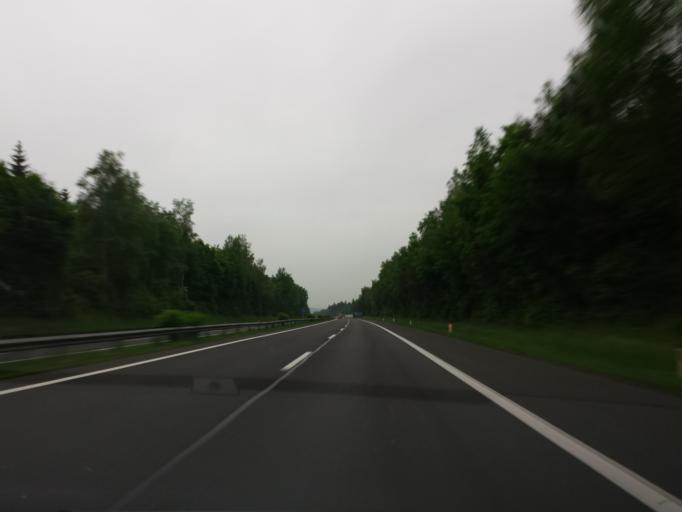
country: AT
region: Styria
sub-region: Politischer Bezirk Hartberg-Fuerstenfeld
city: Bad Waltersdorf
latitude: 47.1257
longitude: 15.9844
